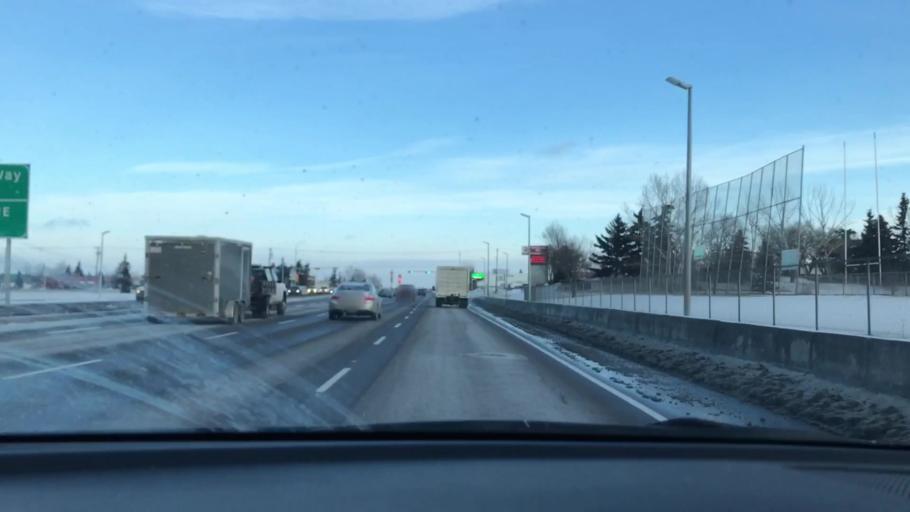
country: CA
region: Alberta
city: Calgary
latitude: 51.0930
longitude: -114.0164
